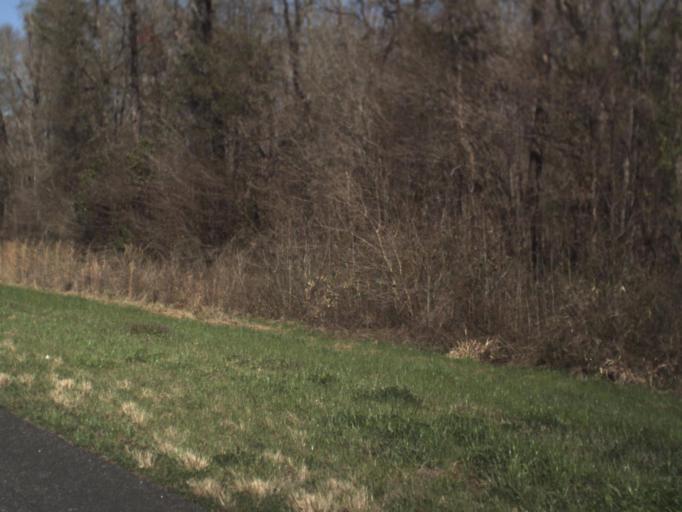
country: US
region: Florida
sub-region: Jackson County
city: Marianna
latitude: 30.8533
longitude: -85.3509
